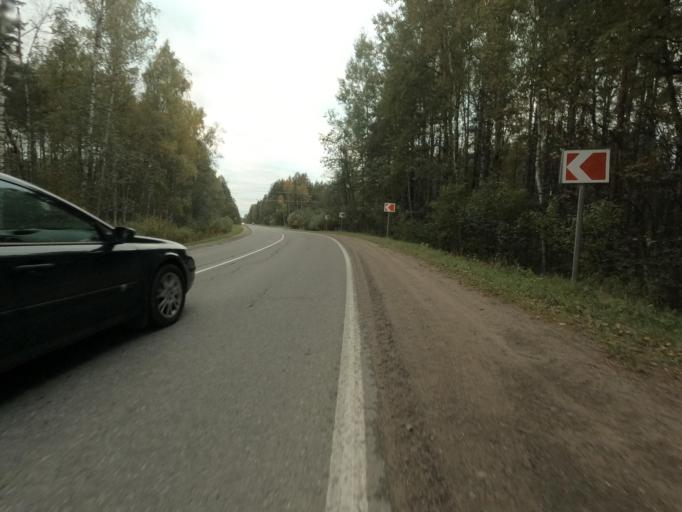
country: RU
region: Leningrad
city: Pavlovo
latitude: 59.8049
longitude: 30.9354
